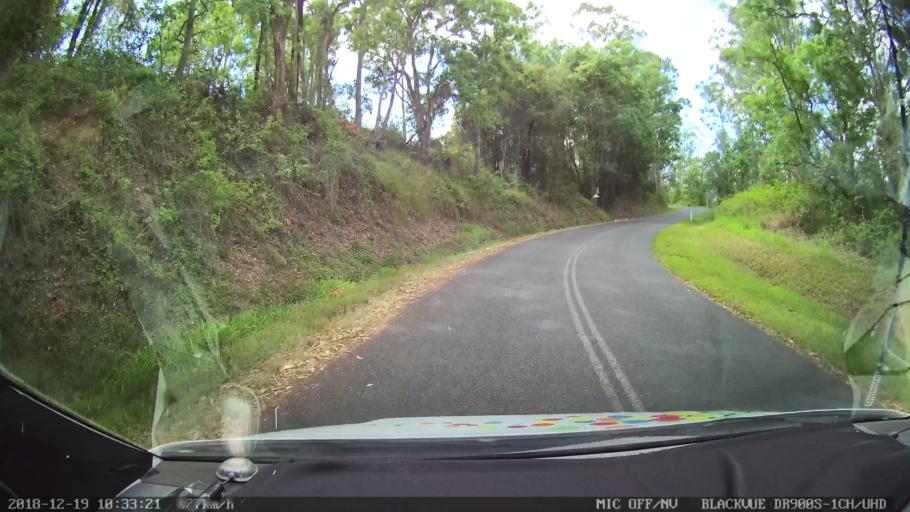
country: AU
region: New South Wales
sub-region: Lismore Municipality
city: Larnook
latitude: -28.5766
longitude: 153.1262
